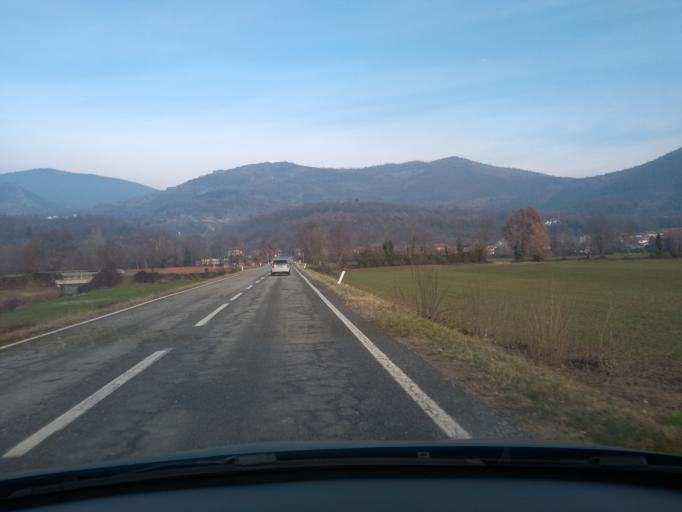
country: IT
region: Piedmont
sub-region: Provincia di Torino
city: Balangero
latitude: 45.2717
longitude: 7.5120
